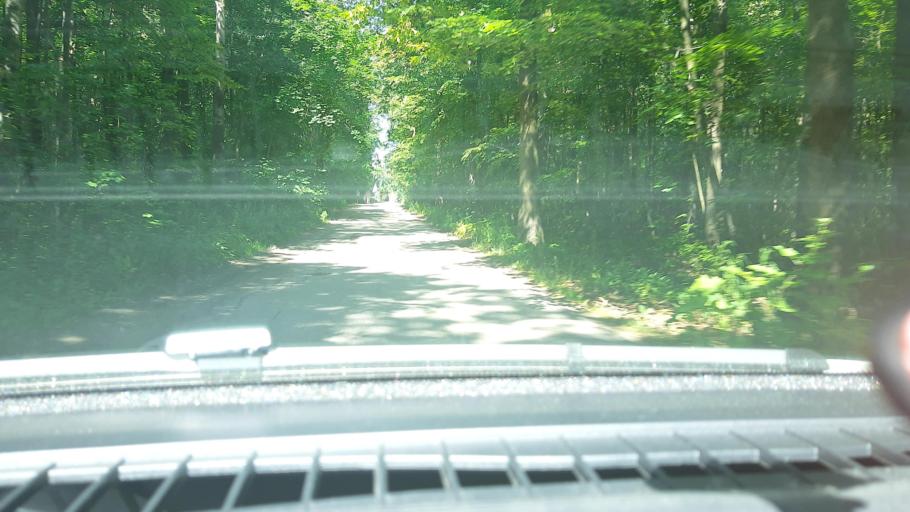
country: RU
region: Nizjnij Novgorod
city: Afonino
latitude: 56.2672
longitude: 44.2017
